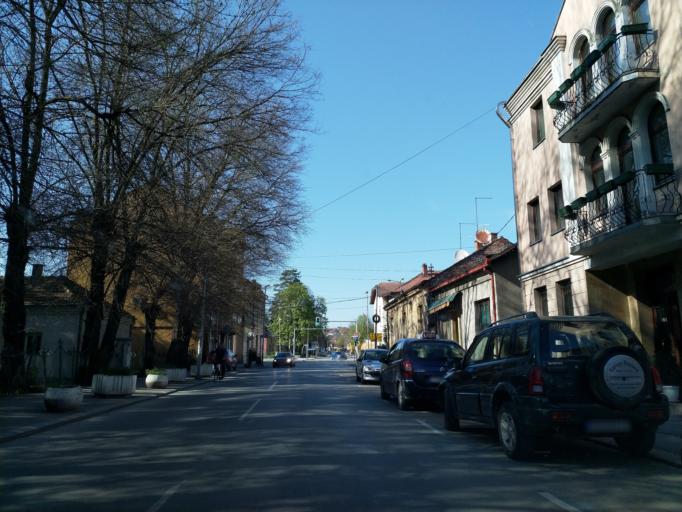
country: RS
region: Central Serbia
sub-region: Kolubarski Okrug
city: Valjevo
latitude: 44.2733
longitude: 19.8838
